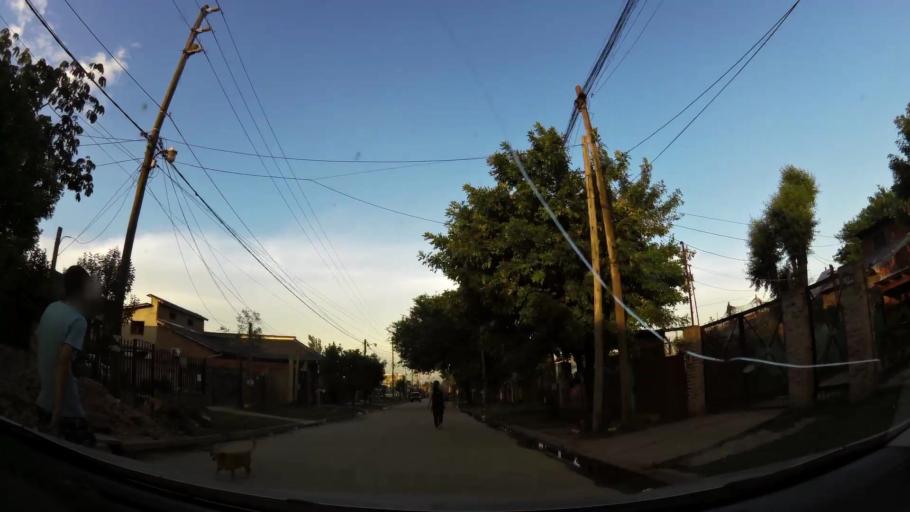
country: AR
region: Buenos Aires
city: Santa Catalina - Dique Lujan
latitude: -34.4324
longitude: -58.6650
